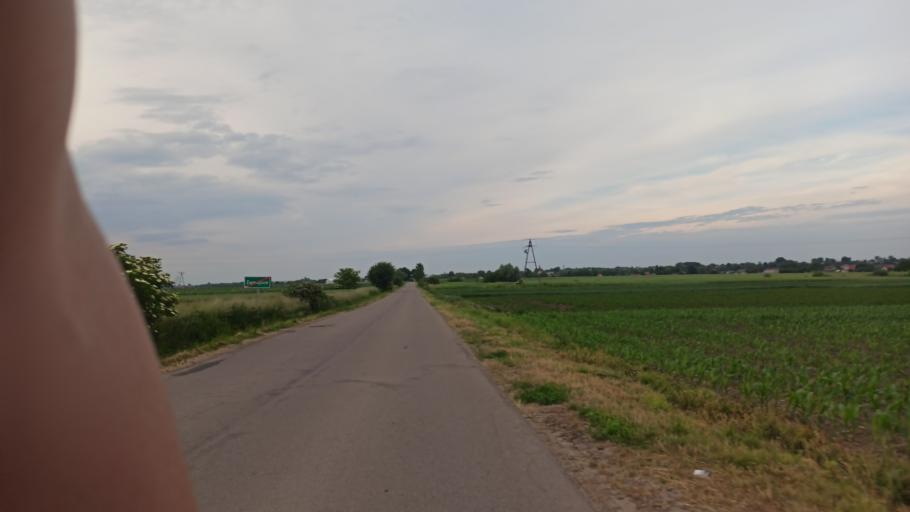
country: PL
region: Subcarpathian Voivodeship
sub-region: Powiat jaroslawski
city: Radymno
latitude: 49.9240
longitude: 22.8015
